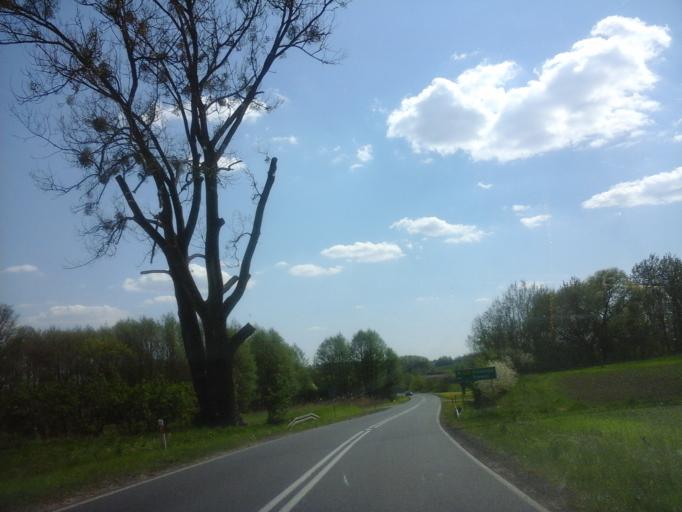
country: PL
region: Lubusz
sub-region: Powiat strzelecko-drezdenecki
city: Dobiegniew
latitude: 52.9859
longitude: 15.7502
